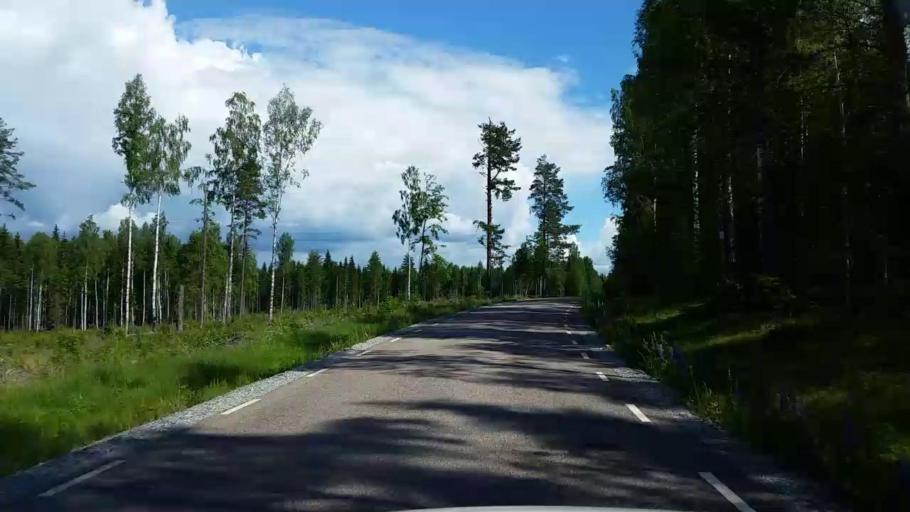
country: SE
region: Vaestmanland
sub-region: Fagersta Kommun
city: Fagersta
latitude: 59.9912
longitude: 15.7415
